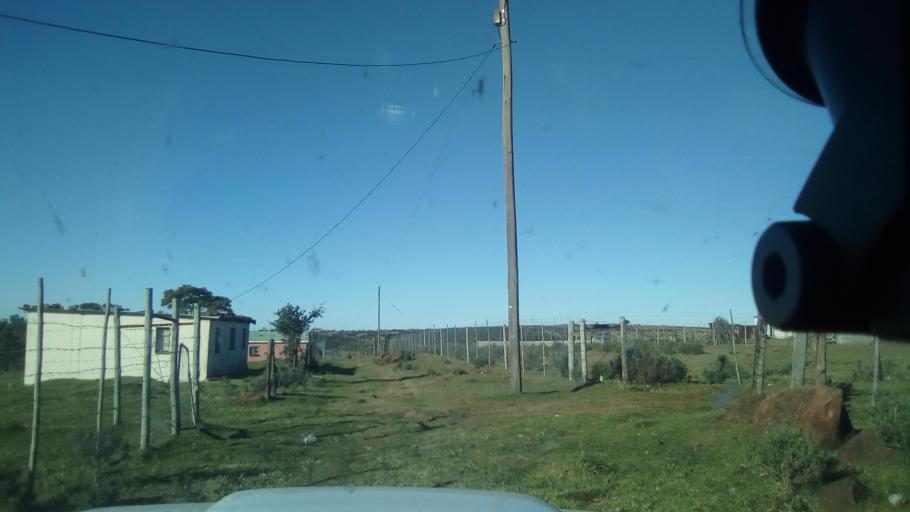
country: ZA
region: Eastern Cape
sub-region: Buffalo City Metropolitan Municipality
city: Bhisho
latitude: -32.9475
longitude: 27.2942
